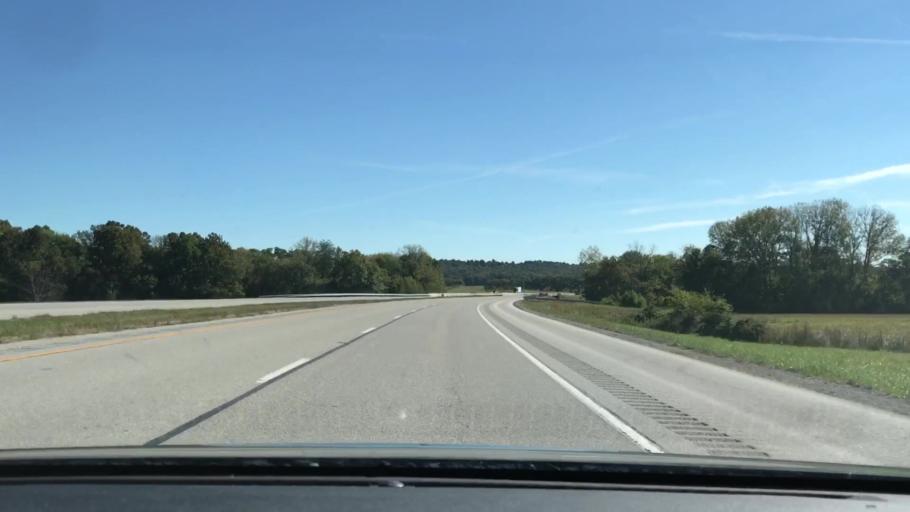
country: US
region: Kentucky
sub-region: Todd County
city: Elkton
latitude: 36.8245
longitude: -87.1578
